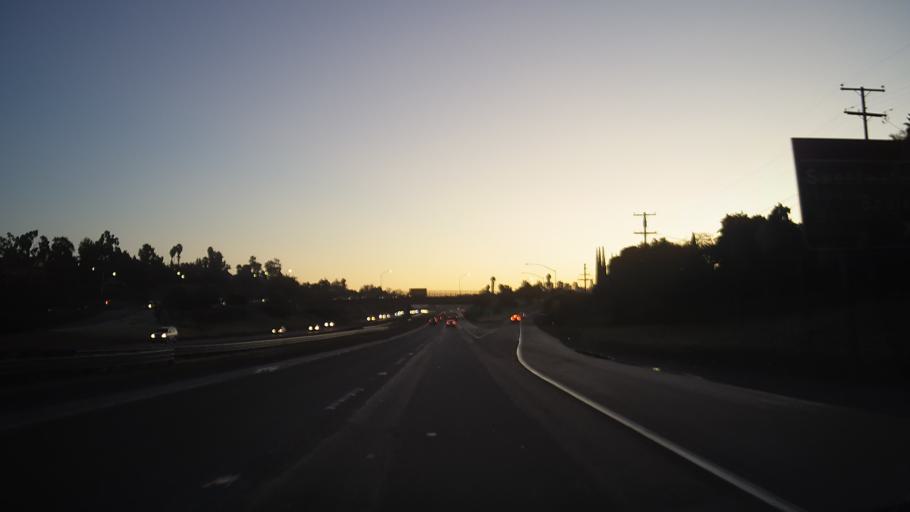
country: US
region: California
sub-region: San Diego County
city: Spring Valley
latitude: 32.7435
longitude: -116.9789
